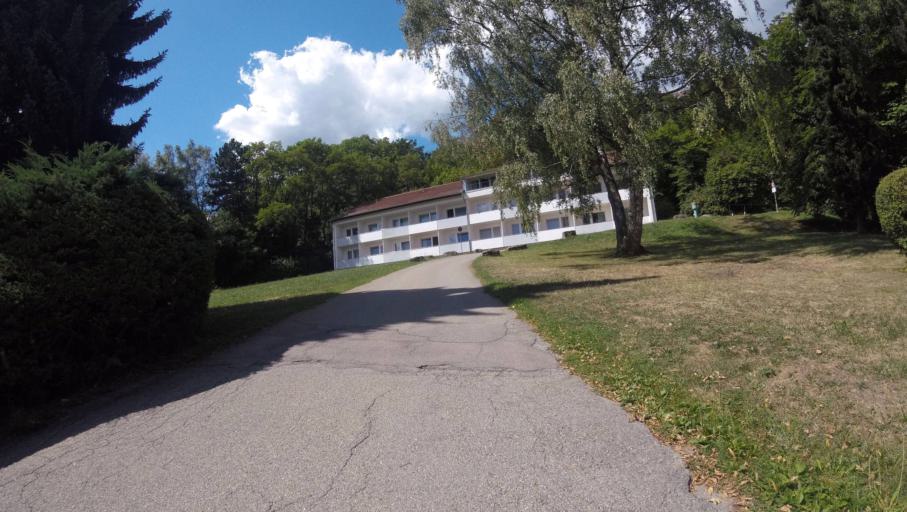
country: DE
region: Baden-Wuerttemberg
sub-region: Regierungsbezirk Stuttgart
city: Oppenweiler
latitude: 49.0069
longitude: 9.4555
